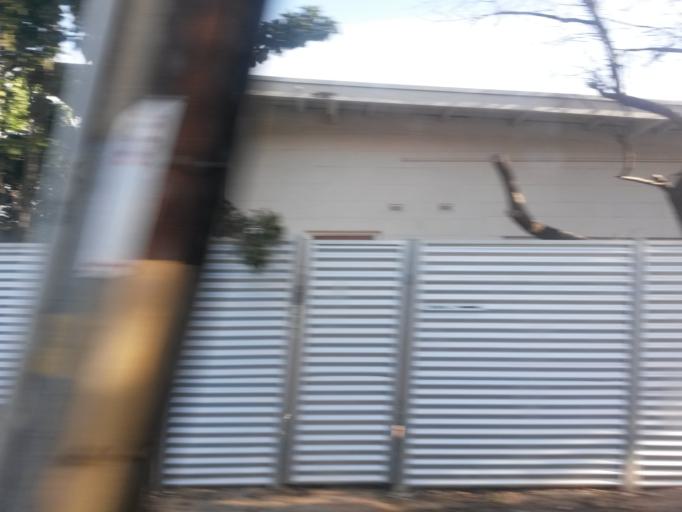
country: AU
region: South Australia
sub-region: Prospect
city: Prospect
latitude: -34.8824
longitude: 138.5720
